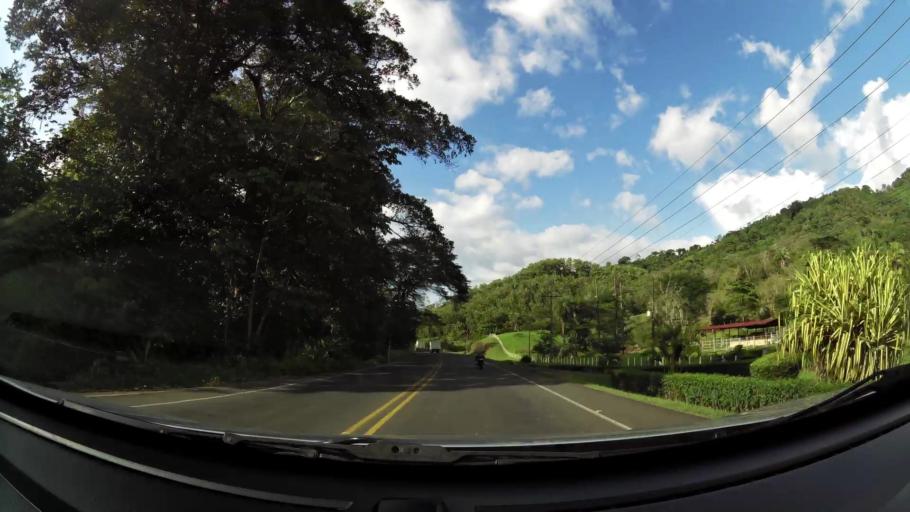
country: CR
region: Puntarenas
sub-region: Canton de Garabito
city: Jaco
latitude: 9.7296
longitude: -84.6263
